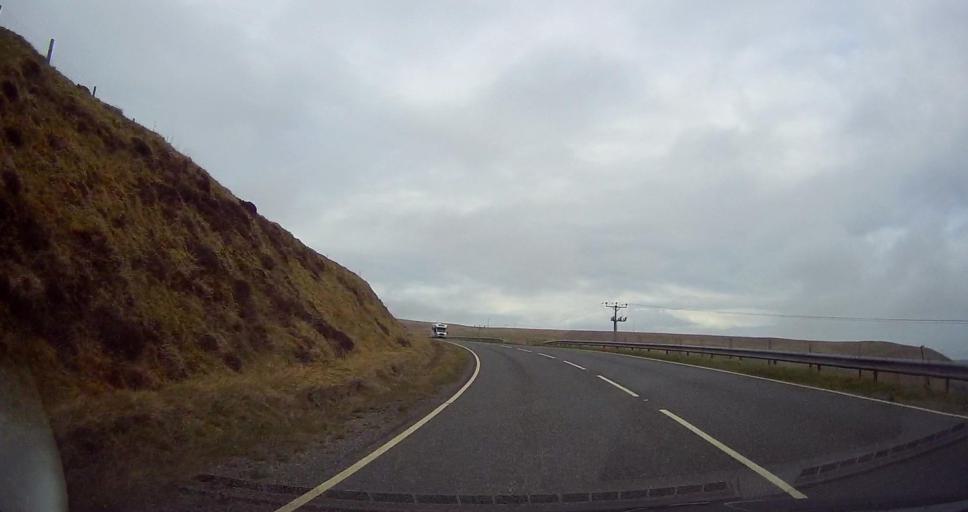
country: GB
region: Scotland
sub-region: Shetland Islands
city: Sandwick
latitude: 59.9914
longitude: -1.2820
